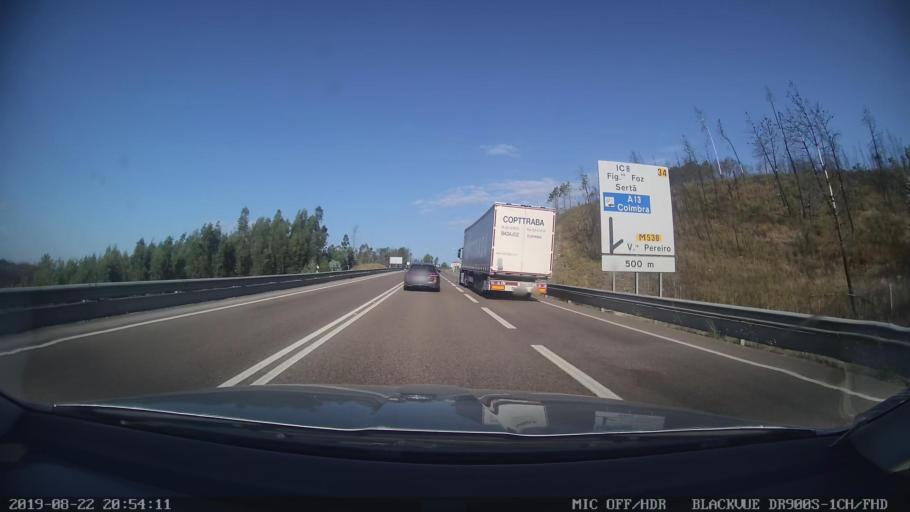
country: PT
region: Castelo Branco
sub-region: Proenca-A-Nova
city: Proenca-a-Nova
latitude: 39.7730
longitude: -8.0091
